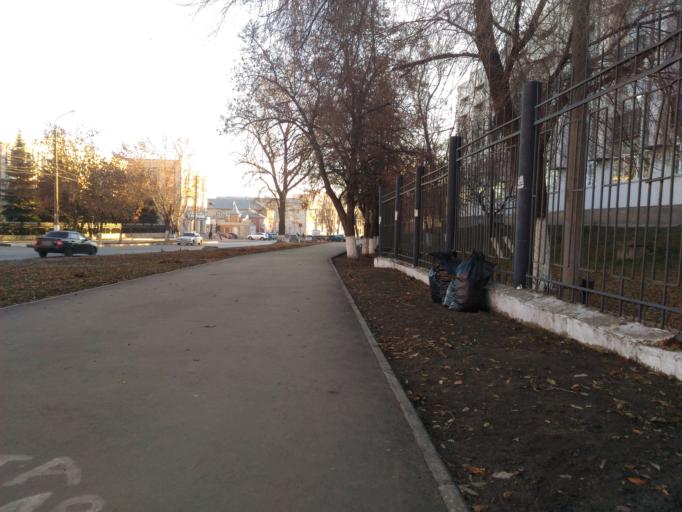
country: RU
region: Ulyanovsk
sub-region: Ulyanovskiy Rayon
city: Ulyanovsk
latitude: 54.3257
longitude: 48.3942
